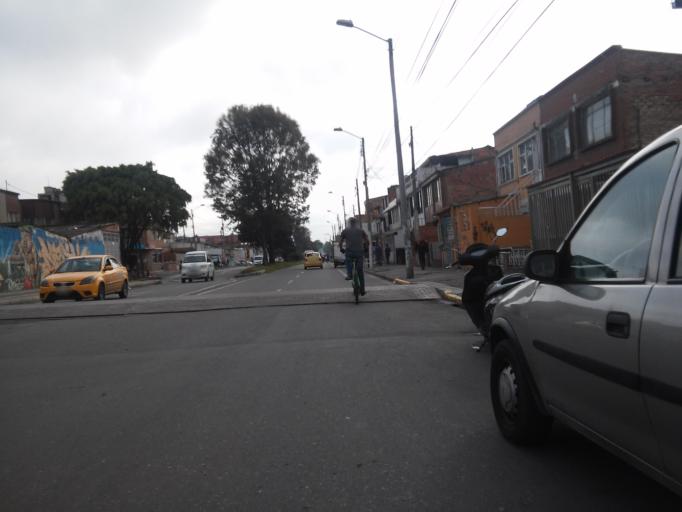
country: CO
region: Bogota D.C.
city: Bogota
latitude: 4.6168
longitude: -74.1474
